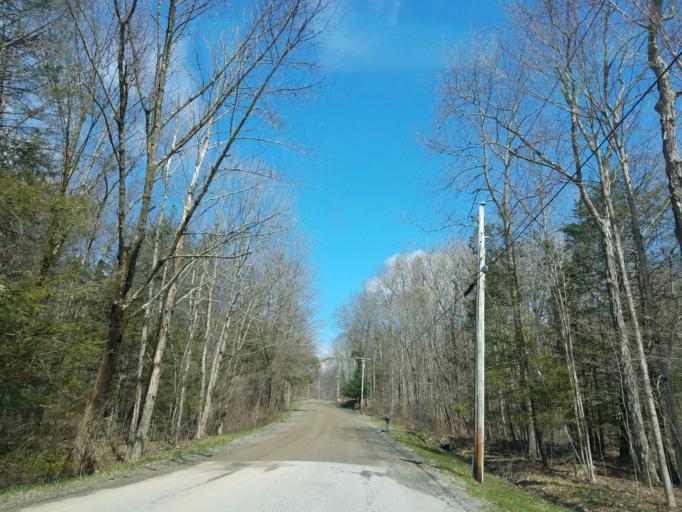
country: US
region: Connecticut
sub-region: Litchfield County
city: West Torrington
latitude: 41.7853
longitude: -73.1654
